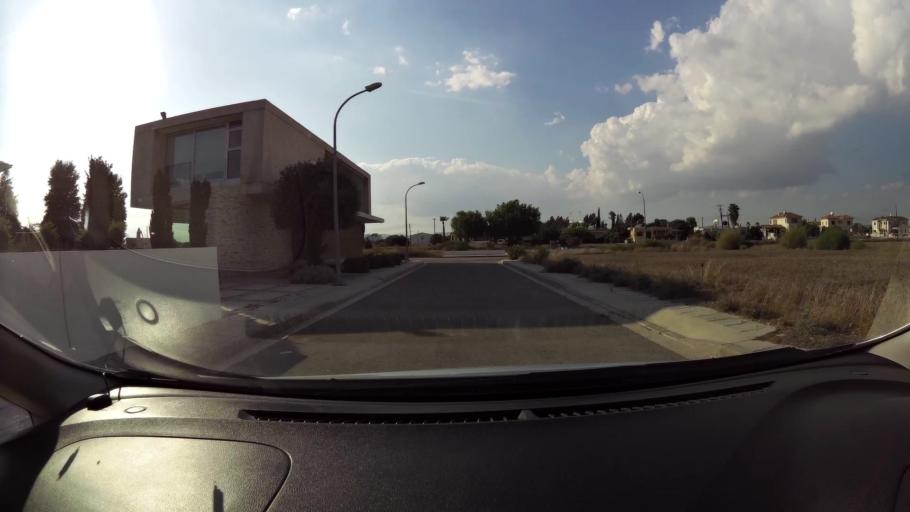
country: CY
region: Larnaka
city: Dhromolaxia
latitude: 34.8807
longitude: 33.5917
